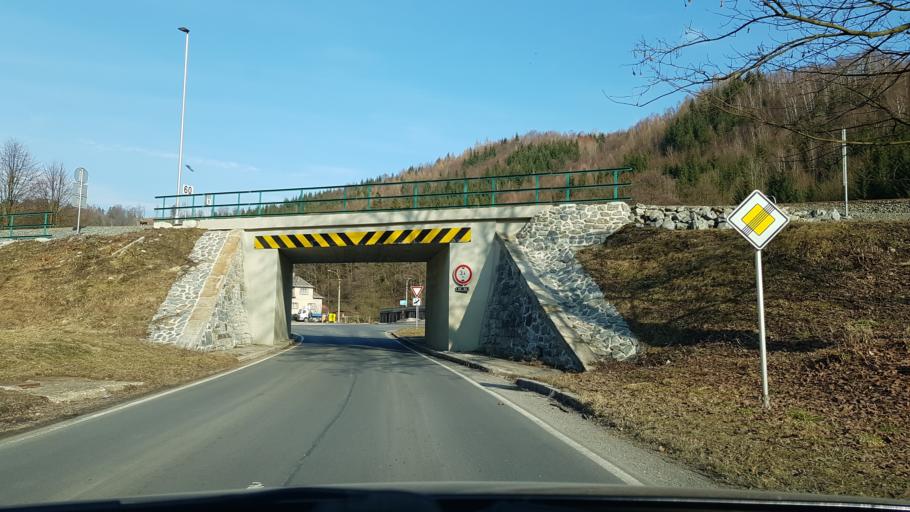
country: CZ
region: Olomoucky
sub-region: Okres Sumperk
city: Hanusovice
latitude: 50.0684
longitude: 16.9293
